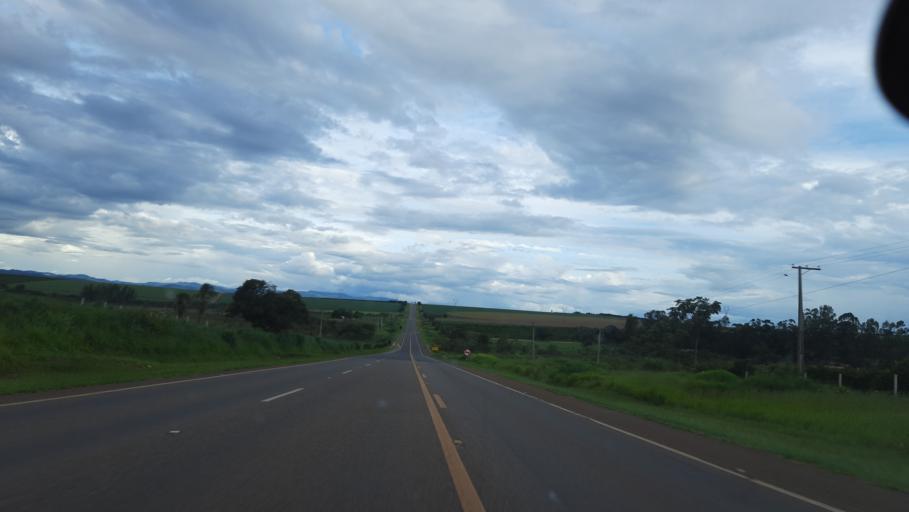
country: BR
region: Sao Paulo
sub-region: Casa Branca
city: Casa Branca
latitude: -21.8044
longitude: -47.0102
